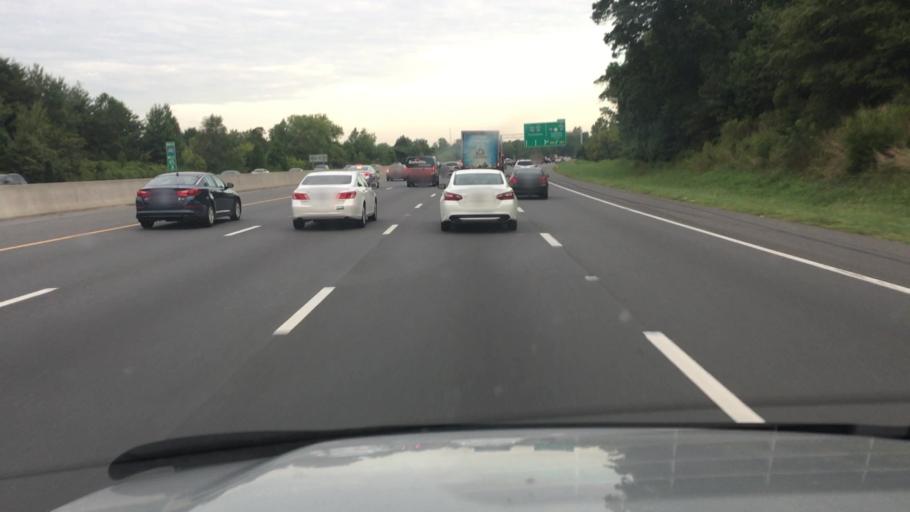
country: US
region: North Carolina
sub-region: Mecklenburg County
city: Pineville
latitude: 35.1065
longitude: -80.8917
